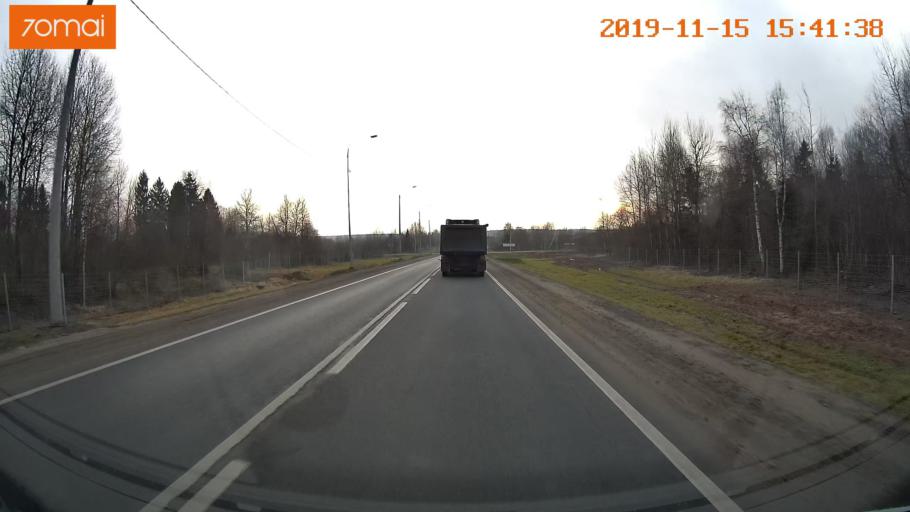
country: RU
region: Jaroslavl
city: Danilov
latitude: 57.9989
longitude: 40.0464
